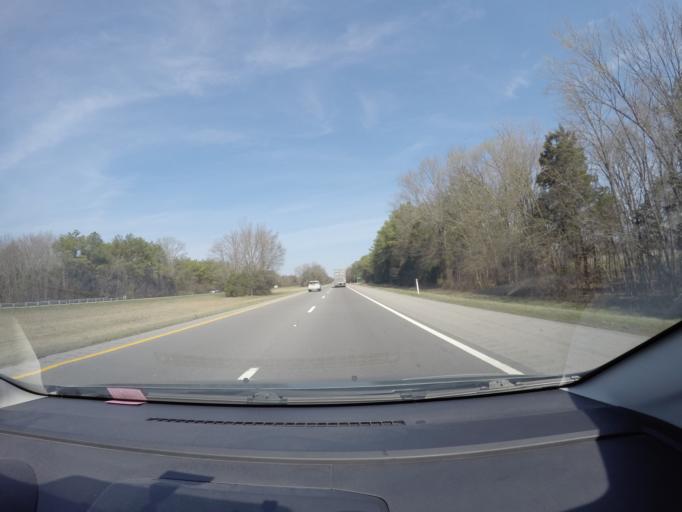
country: US
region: Tennessee
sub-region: Rutherford County
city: Plainview
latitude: 35.7339
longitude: -86.3296
